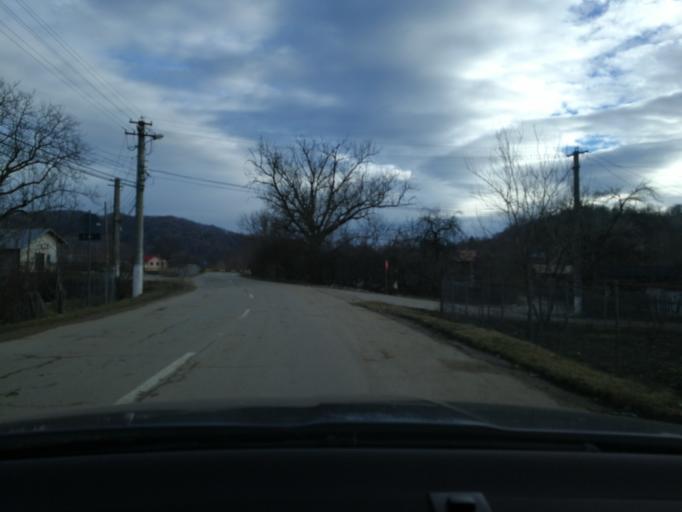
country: RO
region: Prahova
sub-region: Comuna Adunati
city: Ocina de Sus
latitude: 45.1829
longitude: 25.5987
